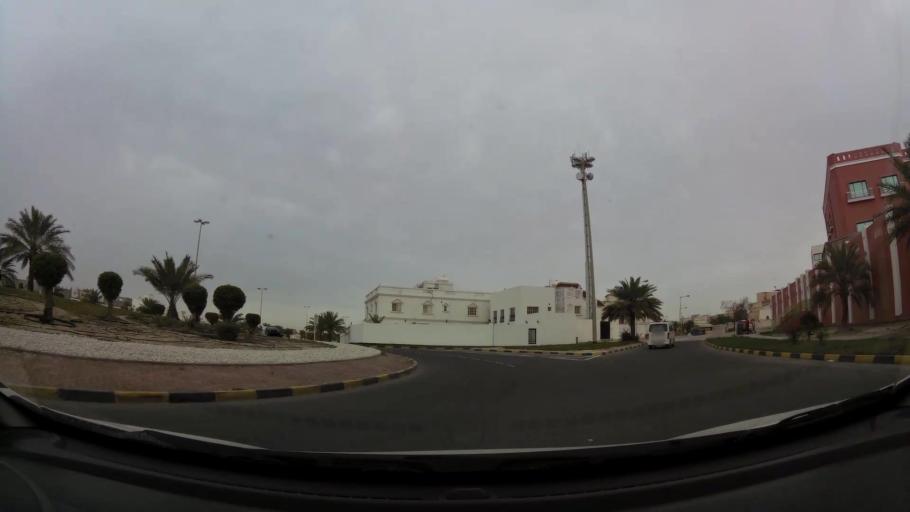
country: BH
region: Central Governorate
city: Madinat Hamad
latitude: 26.0934
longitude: 50.5067
